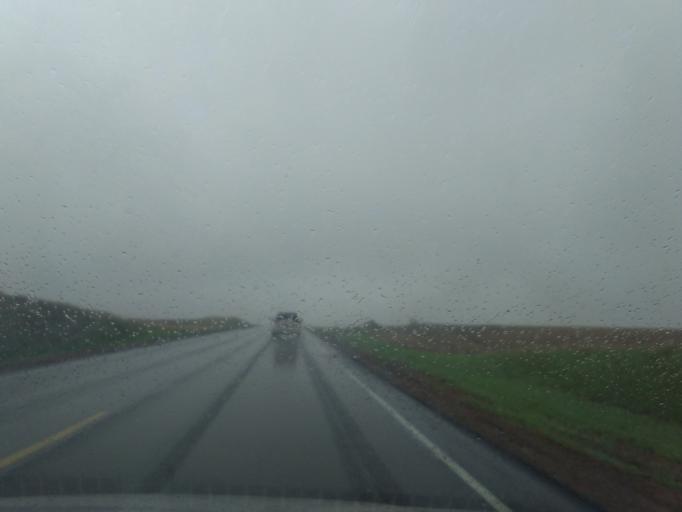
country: US
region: Nebraska
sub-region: Wayne County
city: Wayne
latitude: 42.2173
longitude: -97.1739
